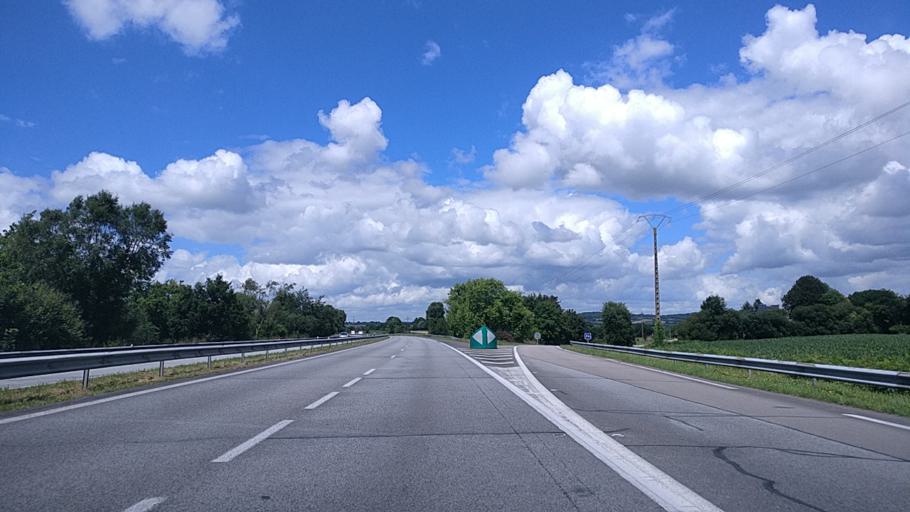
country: FR
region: Brittany
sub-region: Departement du Finistere
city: Briec
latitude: 48.1203
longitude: -4.0227
